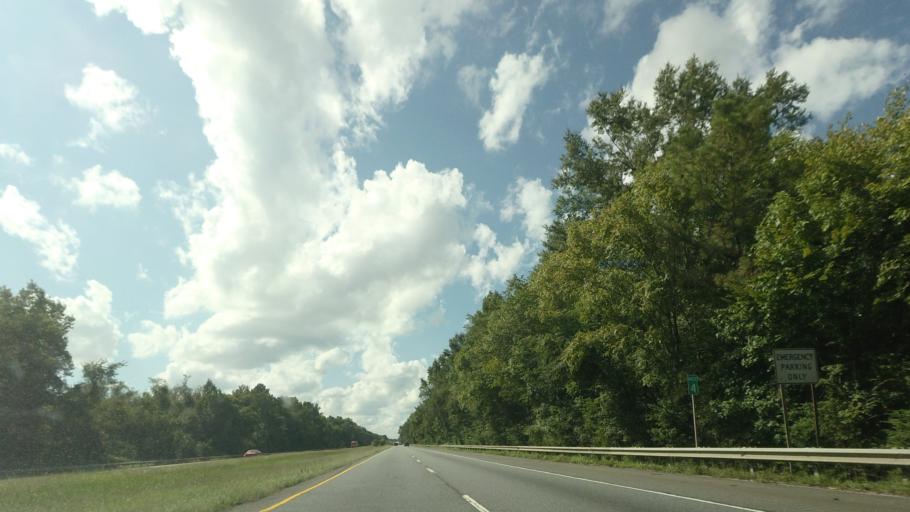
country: US
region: Georgia
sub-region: Bibb County
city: Macon
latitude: 32.8173
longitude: -83.5850
